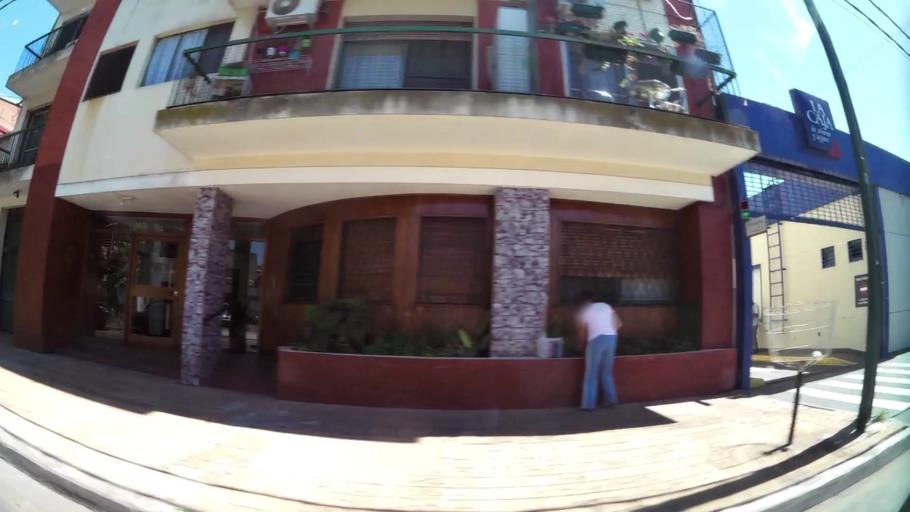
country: AR
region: Buenos Aires
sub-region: Partido de San Isidro
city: San Isidro
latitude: -34.4681
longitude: -58.5187
